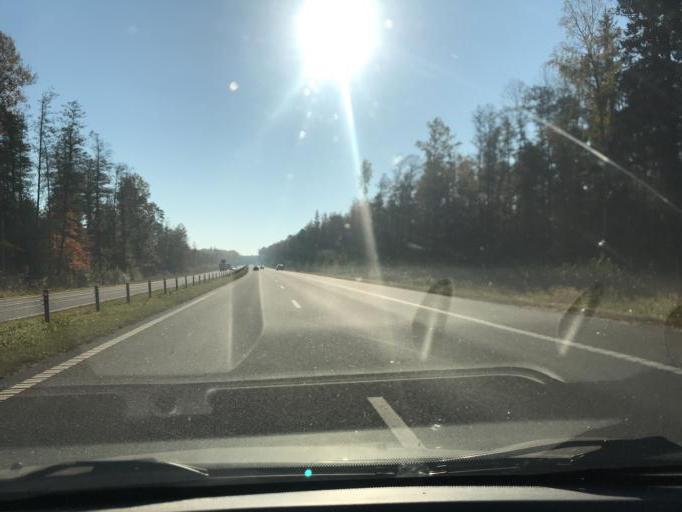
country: BY
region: Minsk
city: Pukhavichy
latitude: 53.4487
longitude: 28.4139
